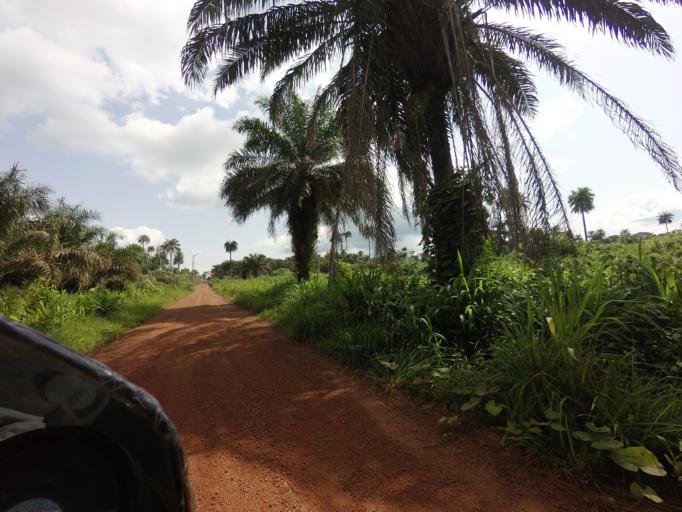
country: SL
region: Eastern Province
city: Daru
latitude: 8.0325
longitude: -10.8814
